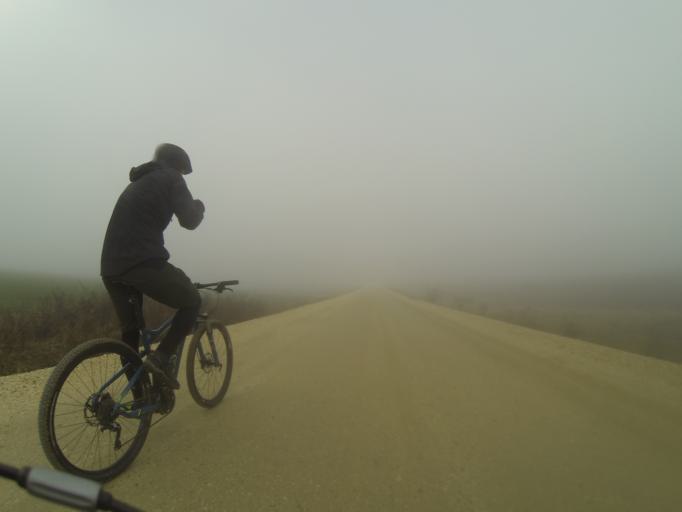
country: RO
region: Mehedinti
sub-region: Comuna Baclesu
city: Baclesu
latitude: 44.4421
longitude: 23.1312
